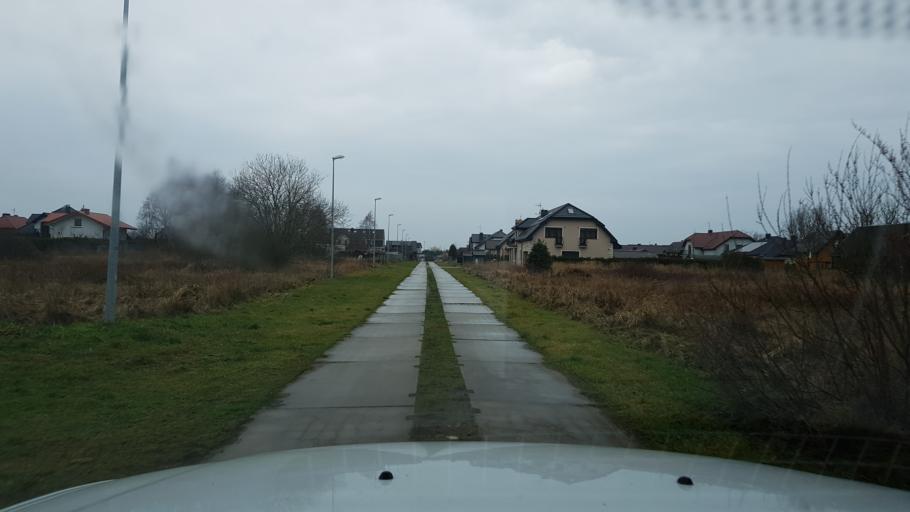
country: PL
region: West Pomeranian Voivodeship
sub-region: Powiat kolobrzeski
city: Grzybowo
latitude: 54.1575
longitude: 15.4977
